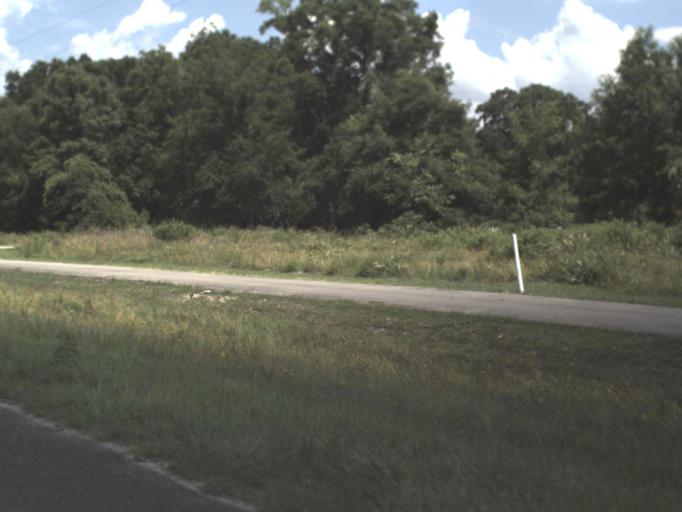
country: US
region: Florida
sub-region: Alachua County
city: High Springs
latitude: 29.9530
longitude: -82.8065
